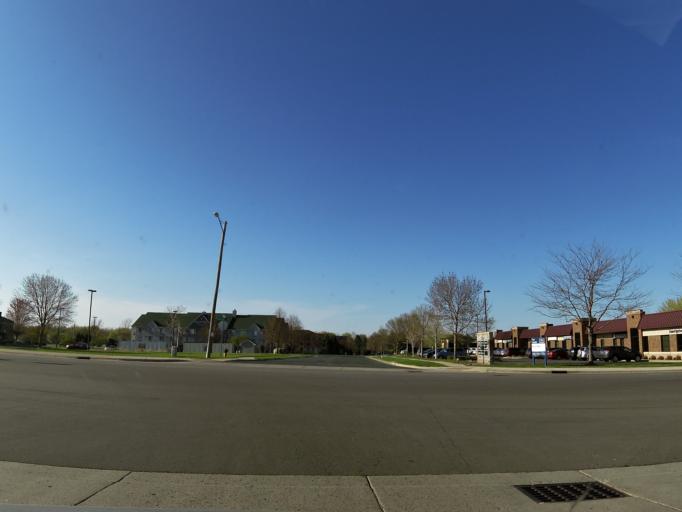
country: US
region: Minnesota
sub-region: Scott County
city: Shakopee
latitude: 44.7808
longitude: -93.5037
